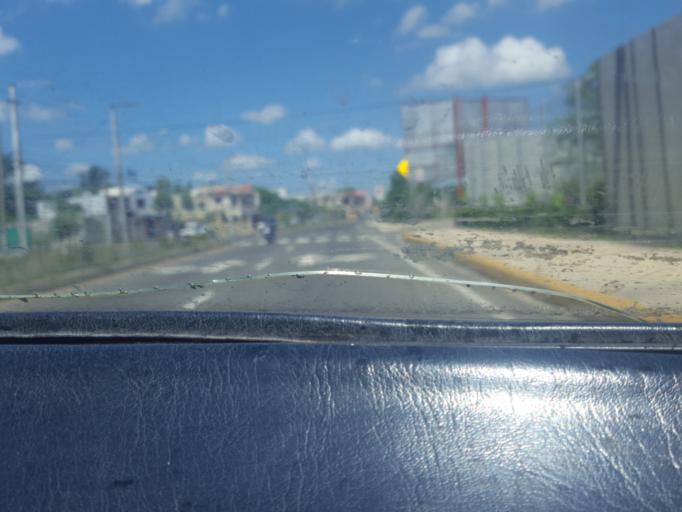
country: DO
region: Santiago
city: Santiago de los Caballeros
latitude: 19.4955
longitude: -70.7004
